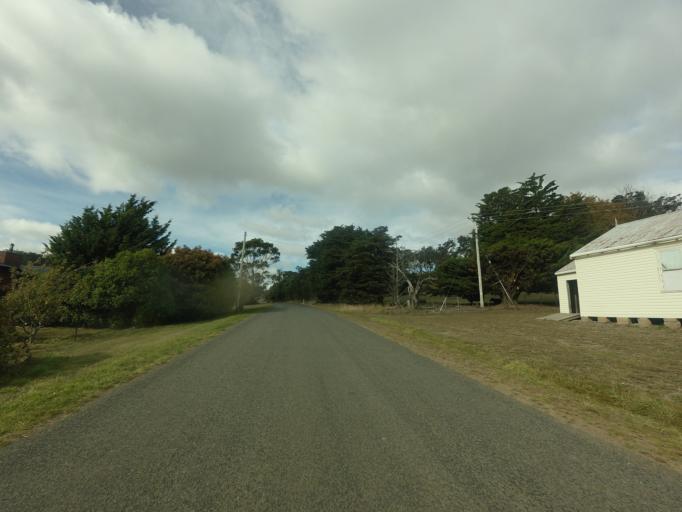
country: AU
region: Tasmania
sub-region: Brighton
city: Bridgewater
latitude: -42.4100
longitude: 147.4008
